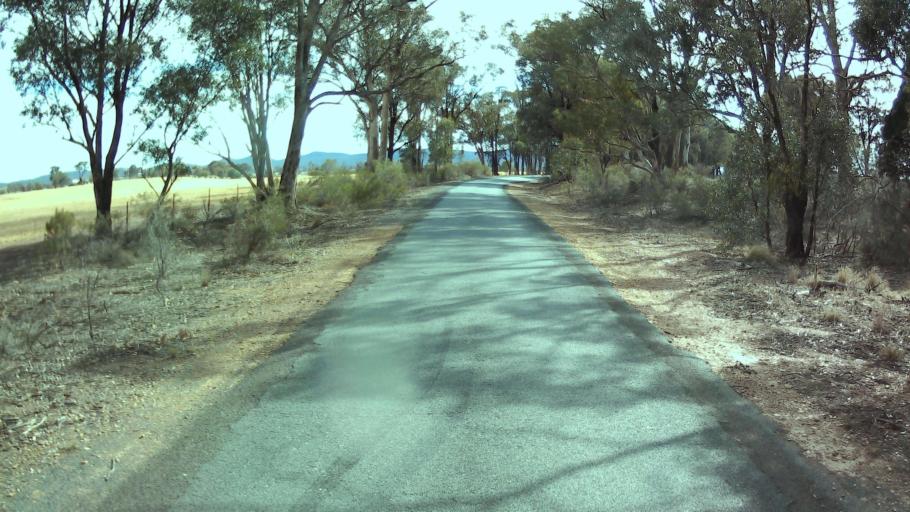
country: AU
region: New South Wales
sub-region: Weddin
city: Grenfell
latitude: -33.8514
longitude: 148.2212
